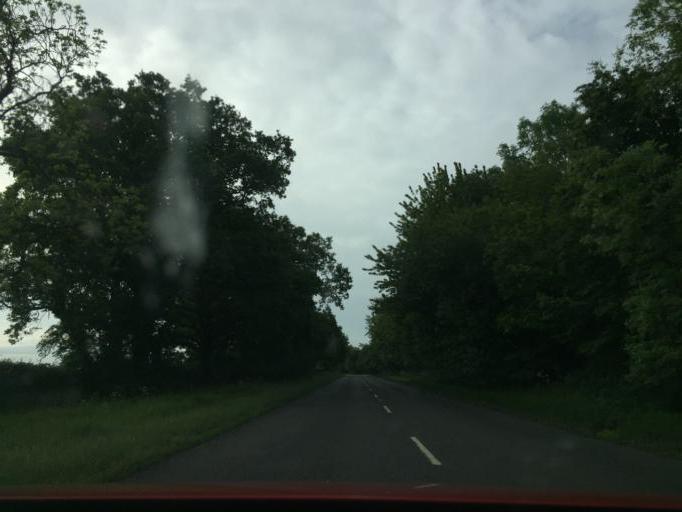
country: GB
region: England
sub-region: Leicestershire
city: Sapcote
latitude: 52.4771
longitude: -1.3261
